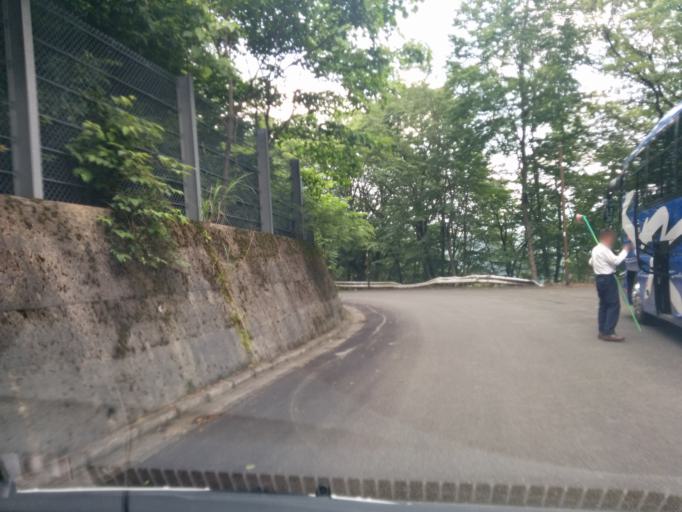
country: JP
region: Kyoto
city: Miyazu
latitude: 35.4497
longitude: 135.1123
